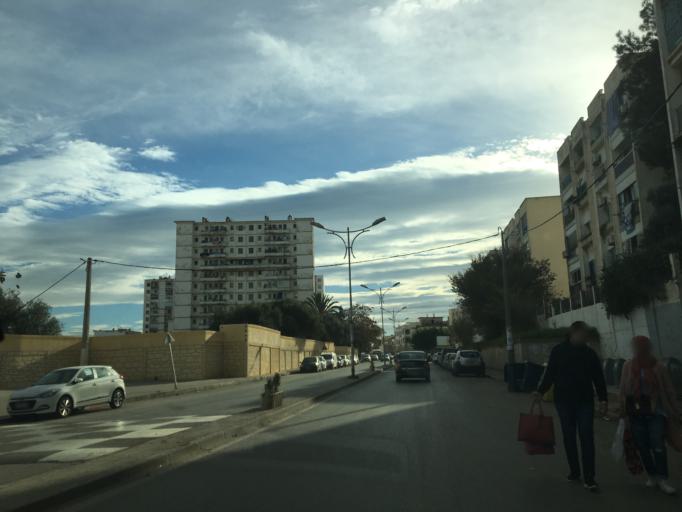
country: DZ
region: Alger
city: Birkhadem
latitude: 36.7347
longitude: 3.0982
